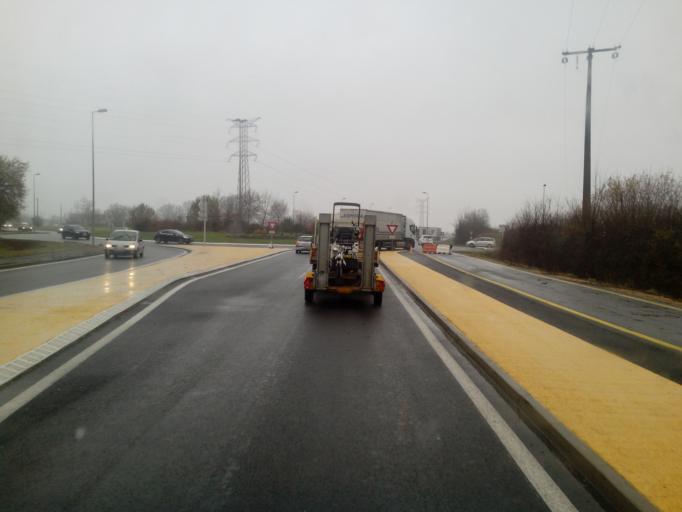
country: FR
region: Poitou-Charentes
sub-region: Departement de la Vienne
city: Mignaloux-Beauvoir
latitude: 46.5529
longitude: 0.4003
